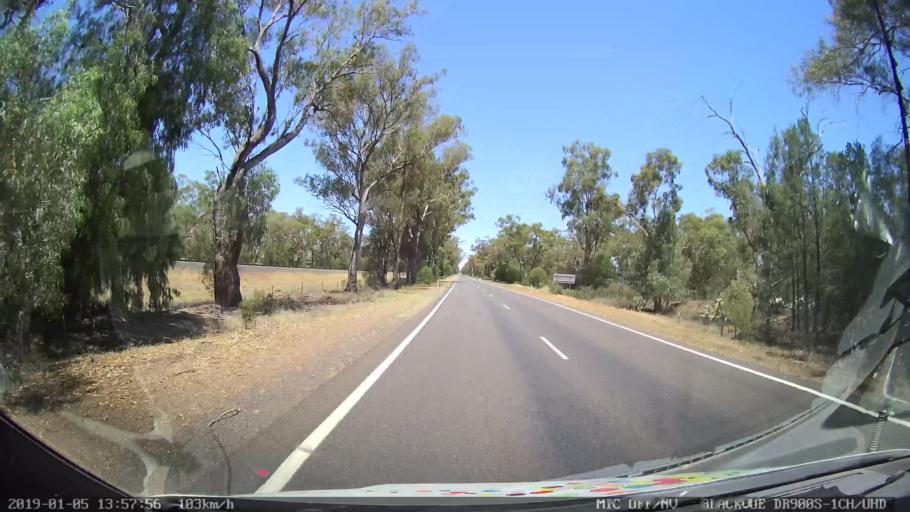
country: AU
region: New South Wales
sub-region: Gunnedah
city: Gunnedah
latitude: -31.1334
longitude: 150.2785
